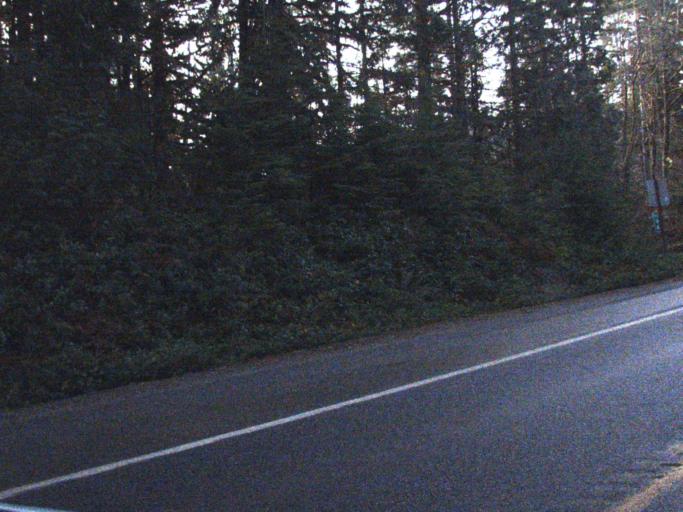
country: US
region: Washington
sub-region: Snohomish County
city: Darrington
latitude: 48.4887
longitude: -121.6260
